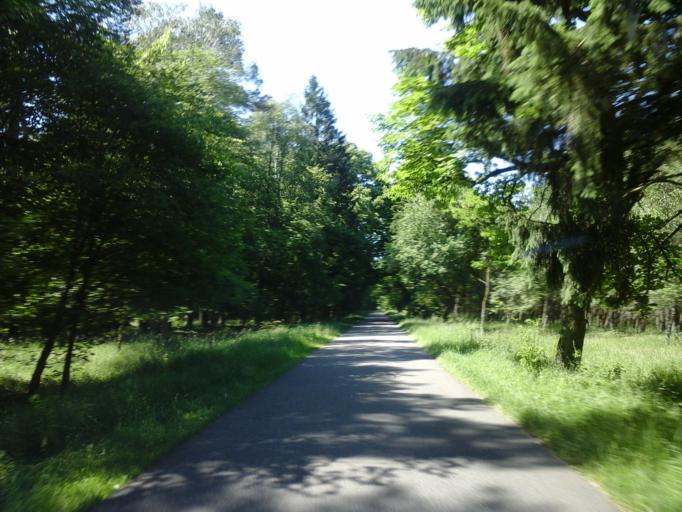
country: PL
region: West Pomeranian Voivodeship
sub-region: Powiat walecki
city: Czlopa
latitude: 53.0714
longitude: 15.9371
